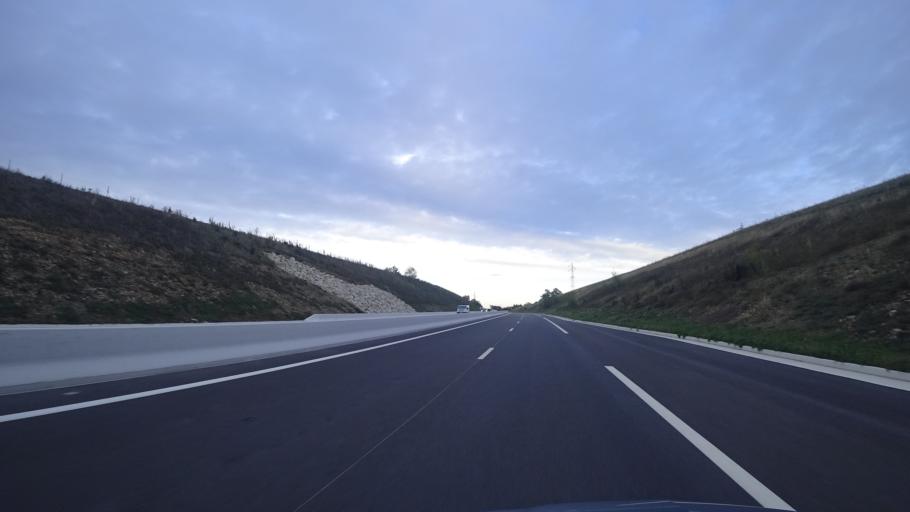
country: FR
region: Midi-Pyrenees
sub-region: Departement de l'Aveyron
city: Baraqueville
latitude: 44.2875
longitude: 2.4702
